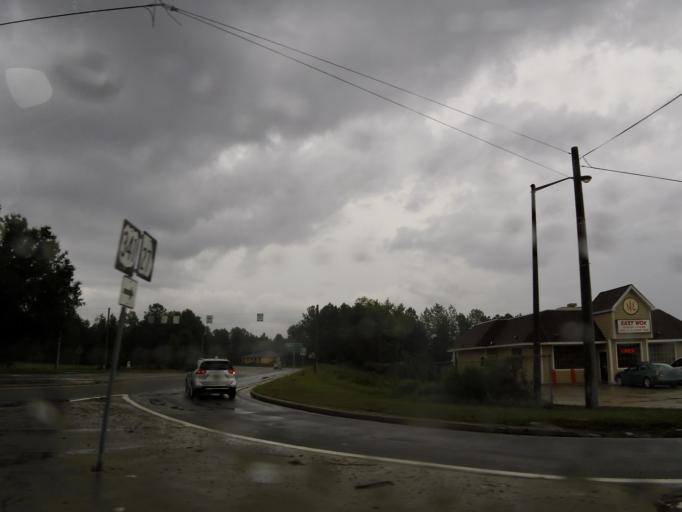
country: US
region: Georgia
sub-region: Wayne County
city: Jesup
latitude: 31.5958
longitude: -81.8713
